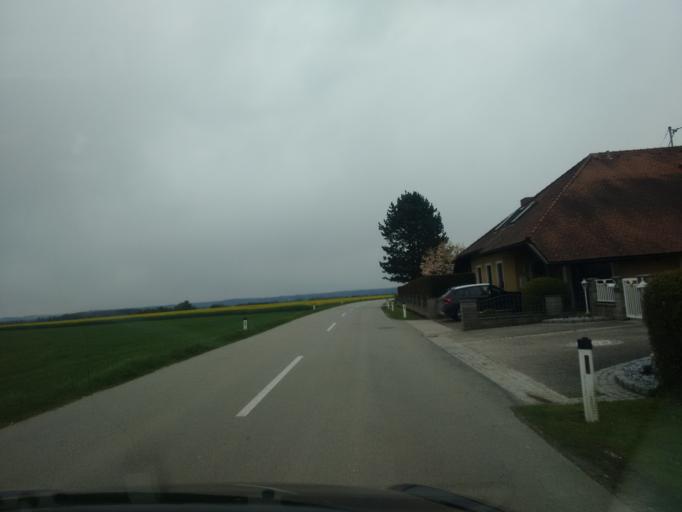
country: AT
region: Upper Austria
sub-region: Wels-Land
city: Holzhausen
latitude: 48.2212
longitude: 14.0762
